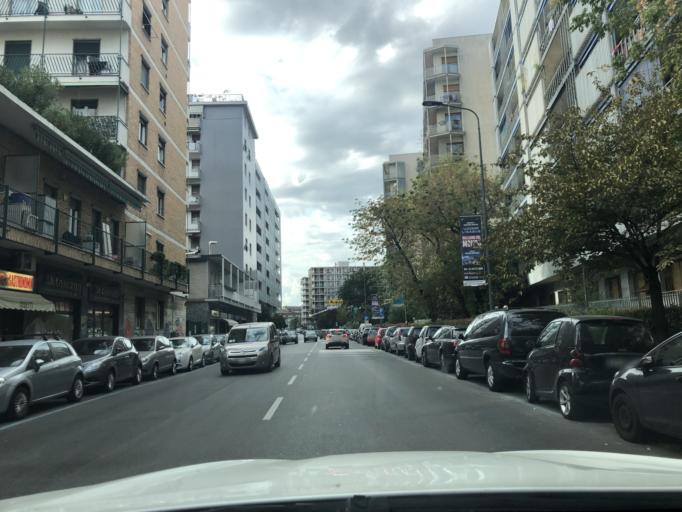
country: IT
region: Lombardy
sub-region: Citta metropolitana di Milano
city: Milano
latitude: 45.4948
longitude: 9.2052
